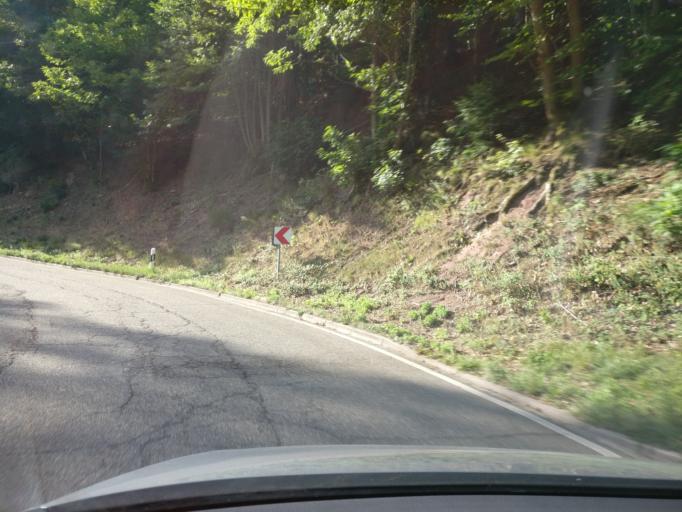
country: DE
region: Baden-Wuerttemberg
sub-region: Karlsruhe Region
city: Loffenau
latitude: 48.7748
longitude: 8.4057
